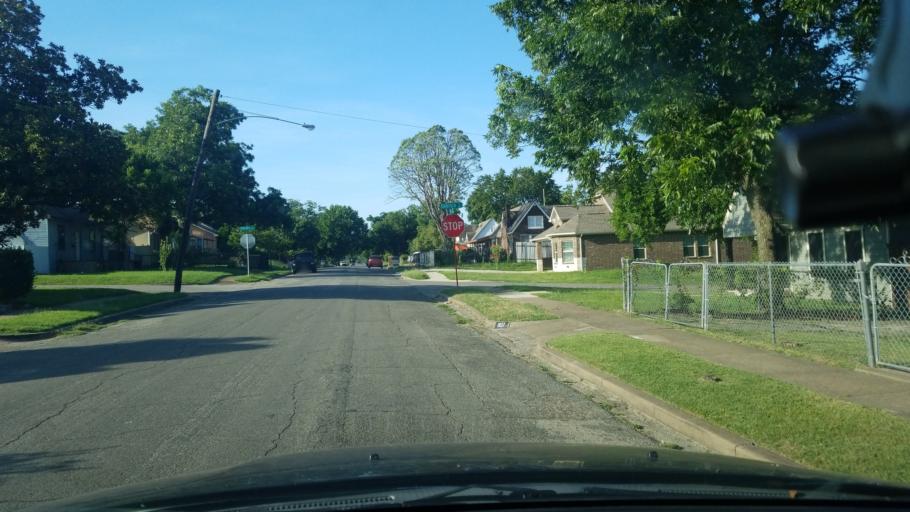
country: US
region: Texas
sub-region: Dallas County
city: Dallas
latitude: 32.7254
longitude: -96.8157
